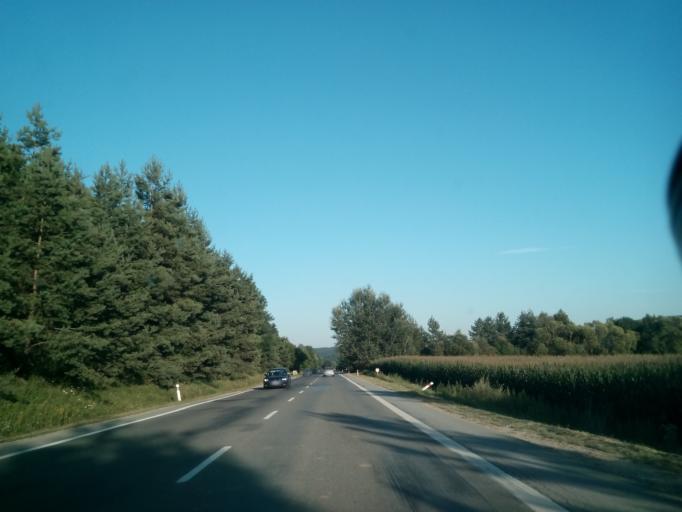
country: SK
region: Presovsky
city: Sabinov
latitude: 49.0150
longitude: 21.0441
